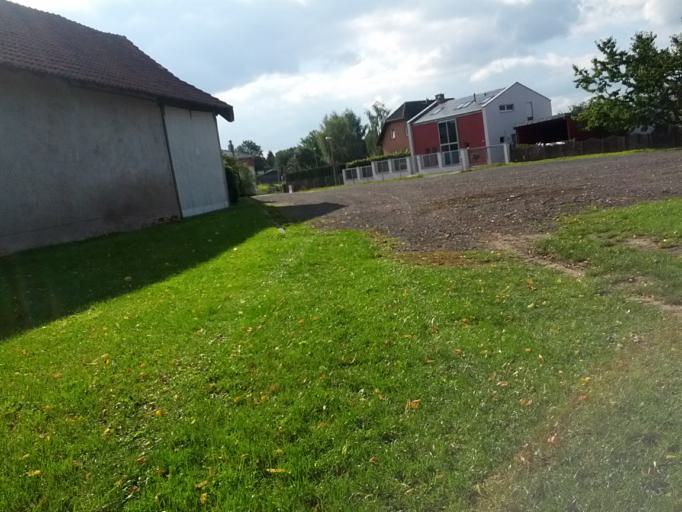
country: DE
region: Thuringia
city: Bischofroda
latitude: 51.0204
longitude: 10.3395
